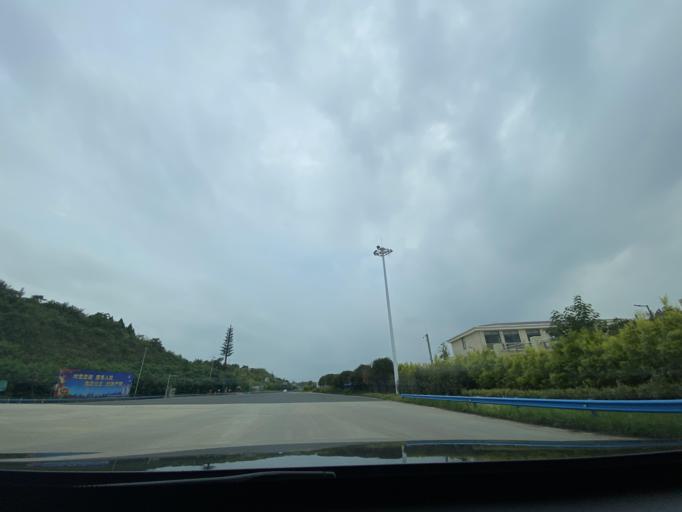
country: CN
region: Sichuan
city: Jiancheng
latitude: 30.4991
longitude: 104.4474
